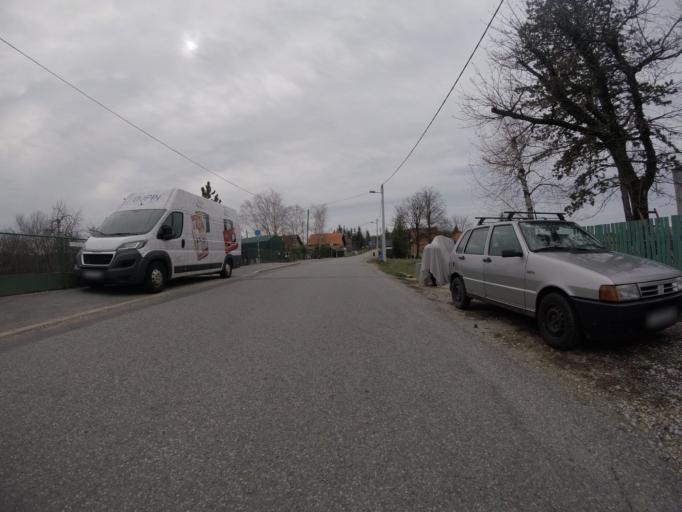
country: HR
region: Grad Zagreb
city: Strmec
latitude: 45.6413
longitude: 15.9352
